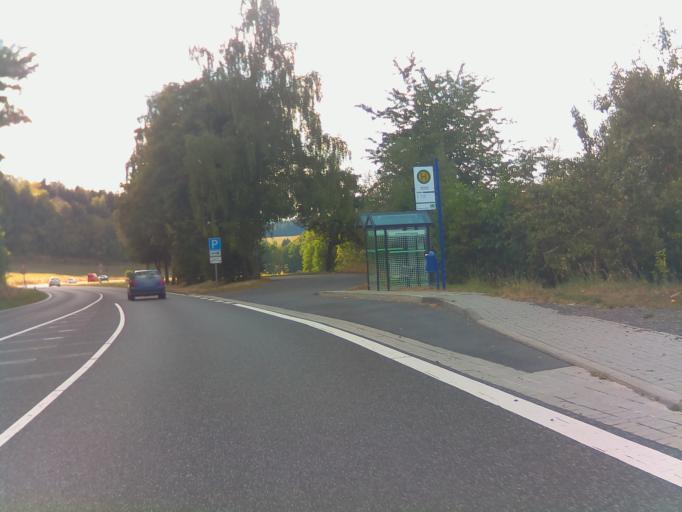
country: DE
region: Hesse
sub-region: Regierungsbezirk Kassel
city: Poppenhausen
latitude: 50.5119
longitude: 9.8703
